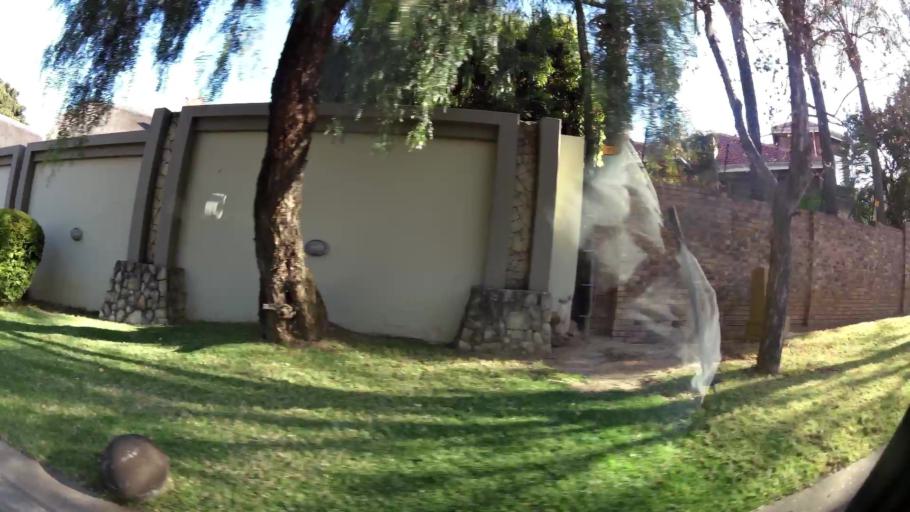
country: ZA
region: Gauteng
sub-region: City of Johannesburg Metropolitan Municipality
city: Roodepoort
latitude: -26.0909
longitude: 27.9583
